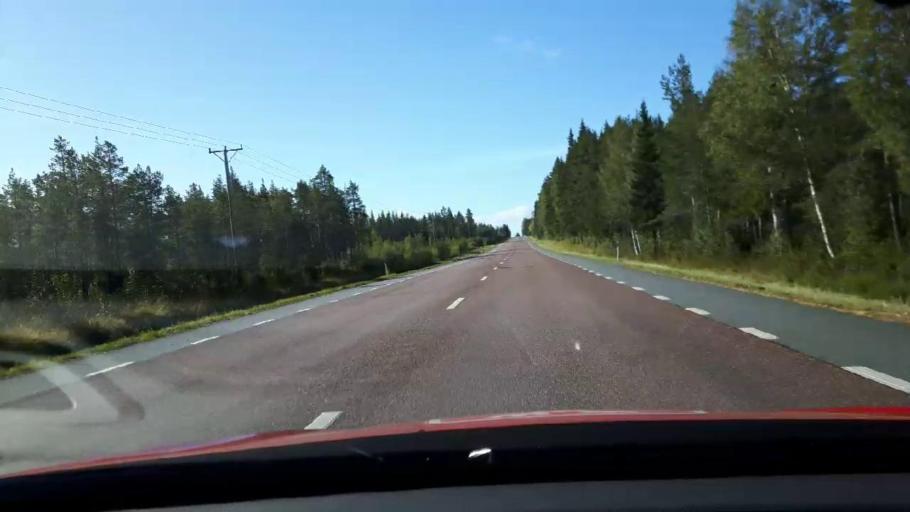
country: SE
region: Jaemtland
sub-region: Braecke Kommun
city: Braecke
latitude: 62.8388
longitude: 15.3205
